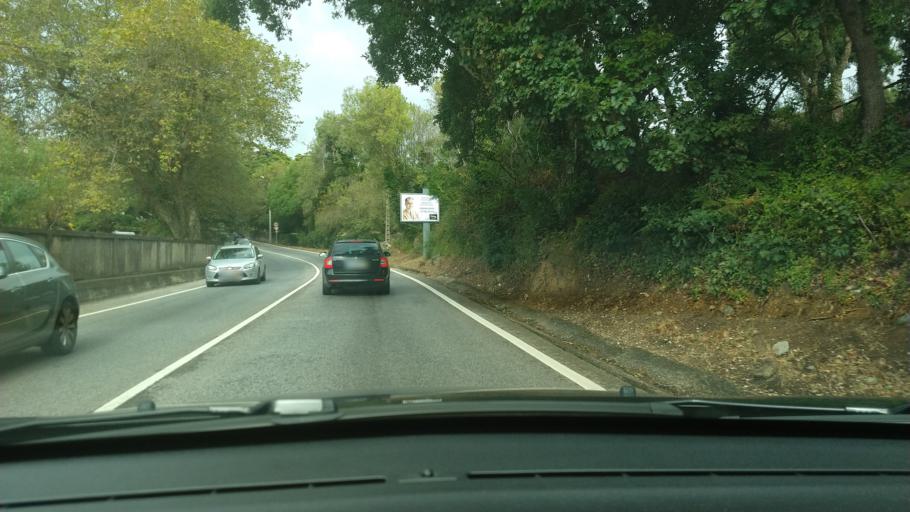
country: PT
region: Lisbon
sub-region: Sintra
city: Sintra
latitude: 38.7852
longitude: -9.3710
